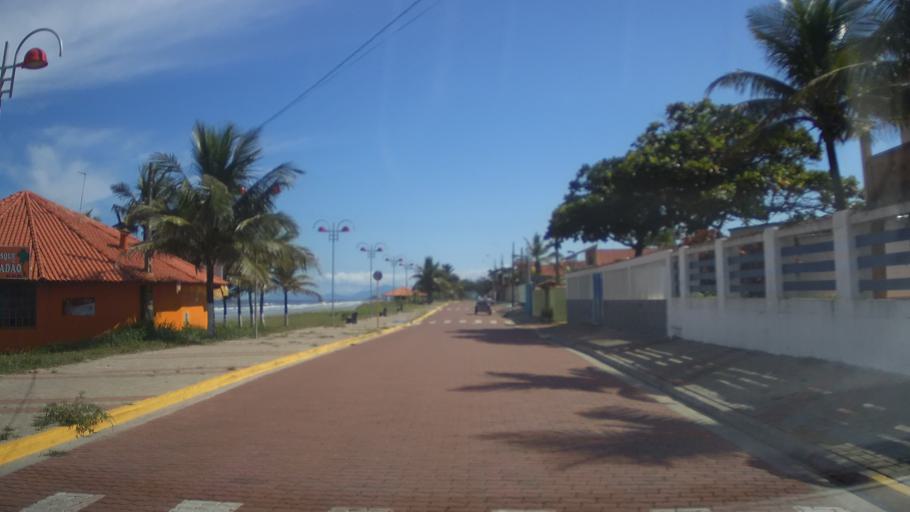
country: BR
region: Sao Paulo
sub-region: Itanhaem
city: Itanhaem
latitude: -24.1695
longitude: -46.7566
